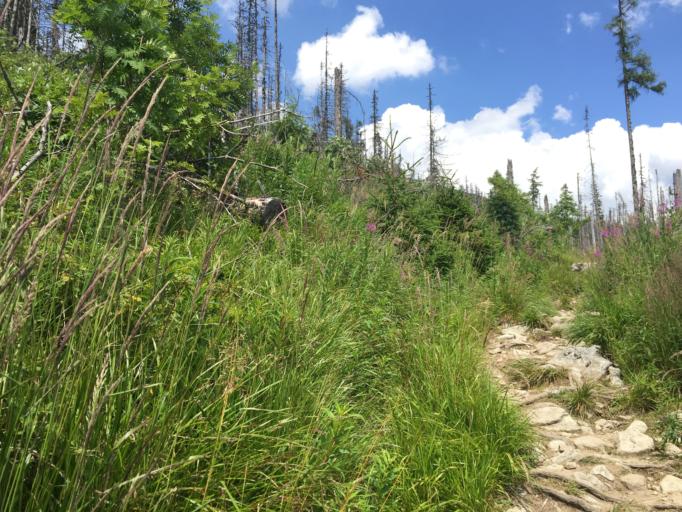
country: SK
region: Presovsky
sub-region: Okres Poprad
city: Vysoke Tatry
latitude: 49.1544
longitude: 20.2105
